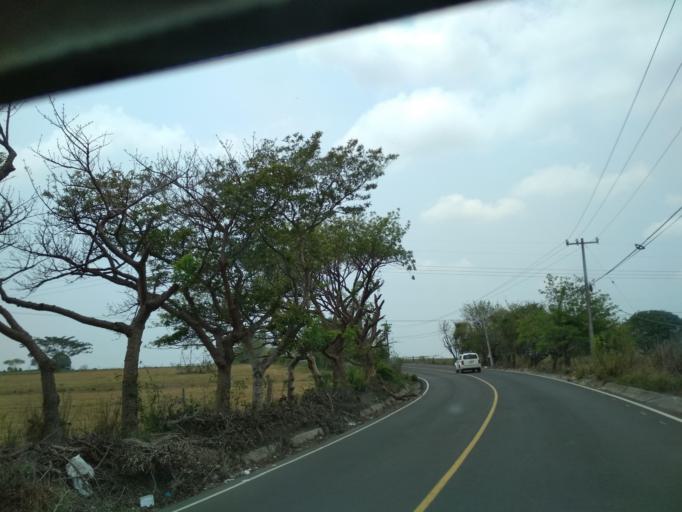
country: MX
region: Veracruz
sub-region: Veracruz
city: Delfino Victoria (Santa Fe)
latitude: 19.1570
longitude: -96.2875
